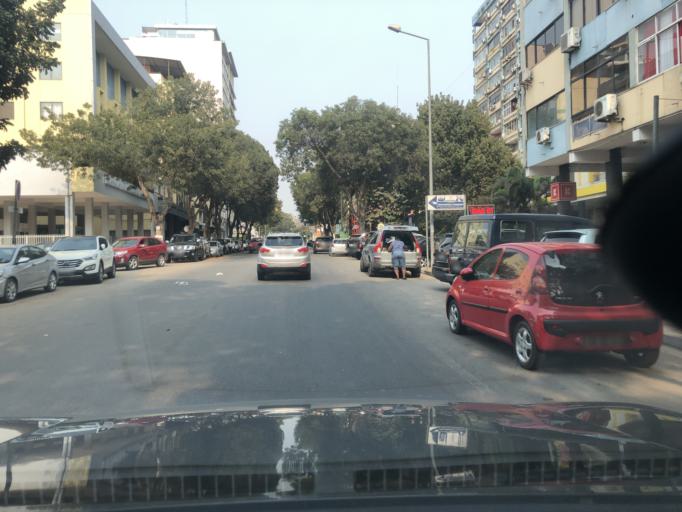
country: AO
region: Luanda
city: Luanda
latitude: -8.8190
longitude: 13.2435
